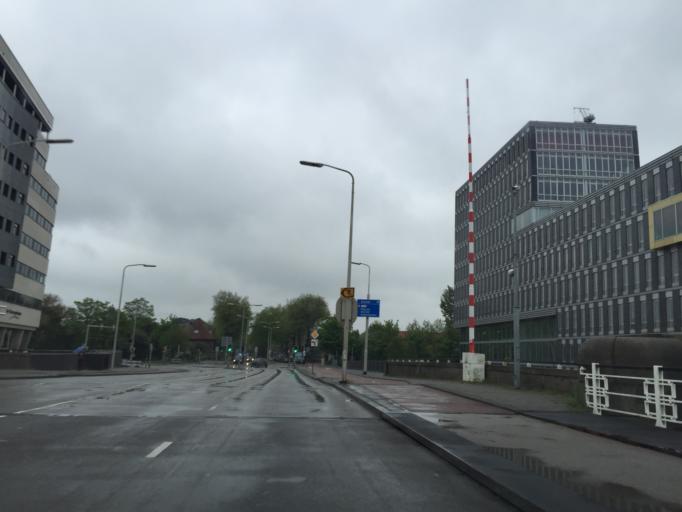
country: NL
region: South Holland
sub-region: Gemeente Leidschendam-Voorburg
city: Voorburg
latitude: 52.0635
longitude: 4.3434
